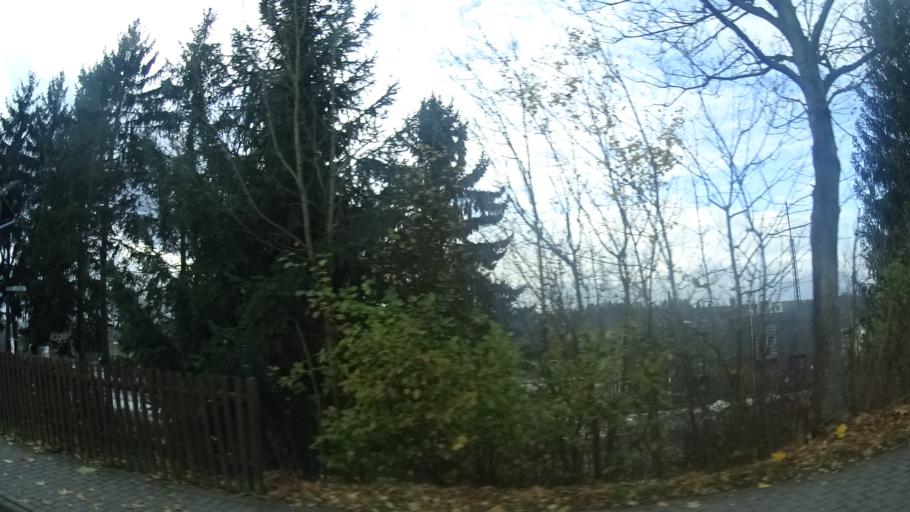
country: DE
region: Hesse
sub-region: Regierungsbezirk Kassel
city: Hunfeld
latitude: 50.6728
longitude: 9.7641
